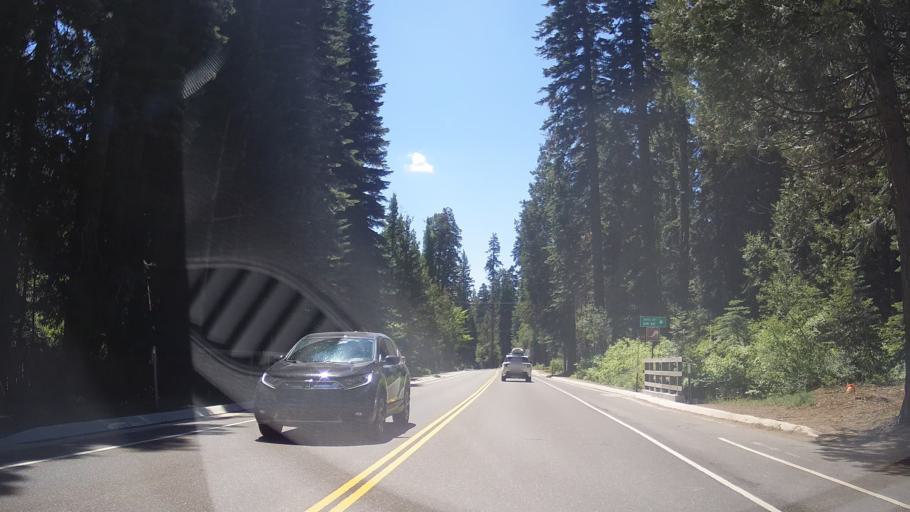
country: US
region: California
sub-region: Placer County
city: Tahoma
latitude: 39.0805
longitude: -120.1576
